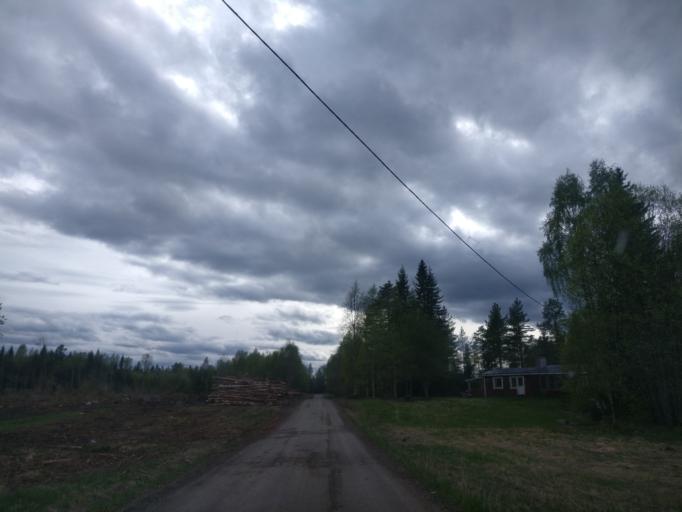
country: SE
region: Vaesternorrland
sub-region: Timra Kommun
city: Soraker
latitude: 62.5163
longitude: 17.5631
